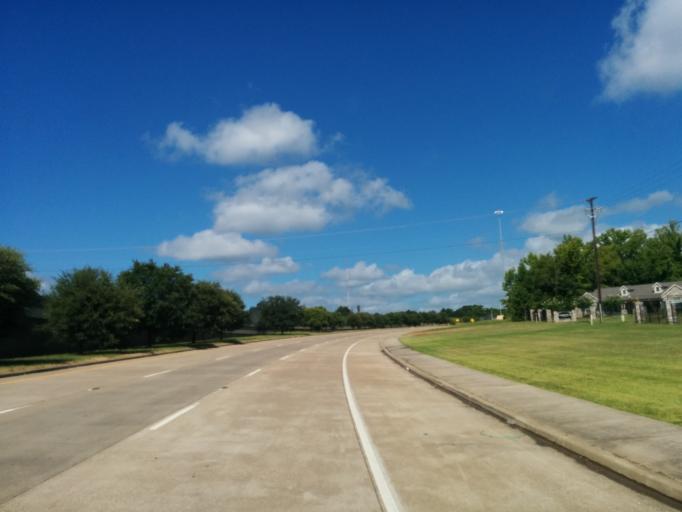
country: US
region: Texas
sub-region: Angelina County
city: Lufkin
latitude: 31.3682
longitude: -94.7506
